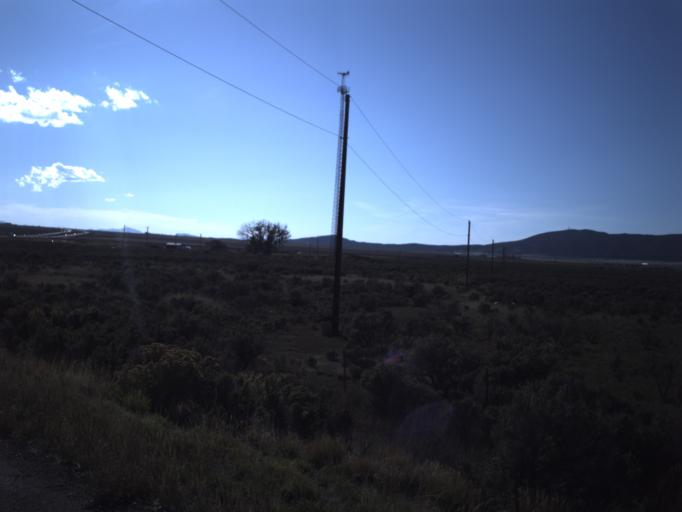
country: US
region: Utah
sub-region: Iron County
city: Parowan
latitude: 37.8400
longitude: -112.8722
